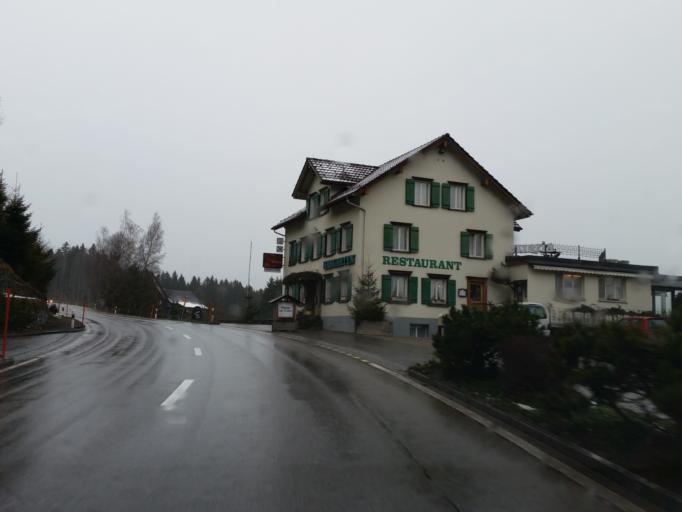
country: CH
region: Appenzell Innerrhoden
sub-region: Appenzell Inner Rhodes
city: Gonten
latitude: 47.3555
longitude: 9.3547
